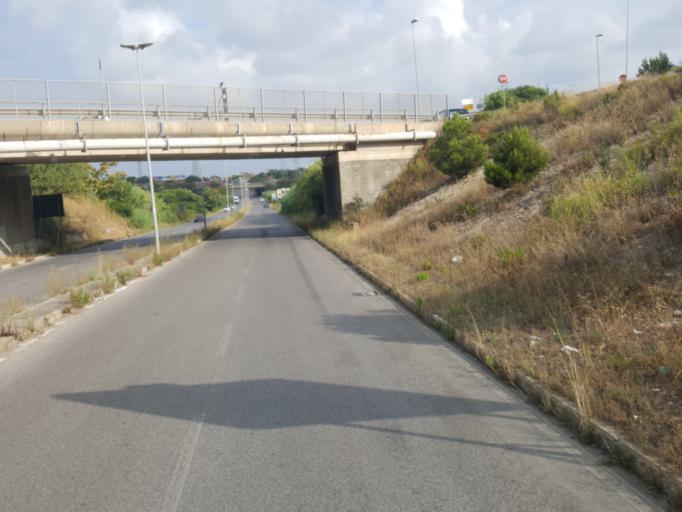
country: IT
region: Latium
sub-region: Citta metropolitana di Roma Capitale
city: Civitavecchia
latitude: 42.1029
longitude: 11.7929
